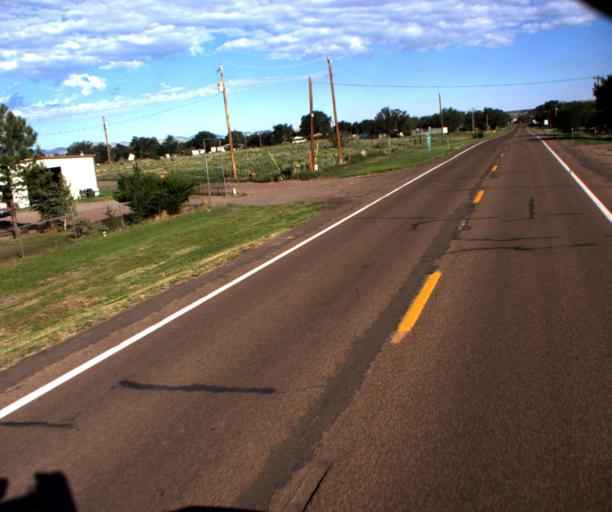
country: US
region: Arizona
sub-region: Apache County
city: Springerville
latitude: 34.1280
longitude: -109.2659
